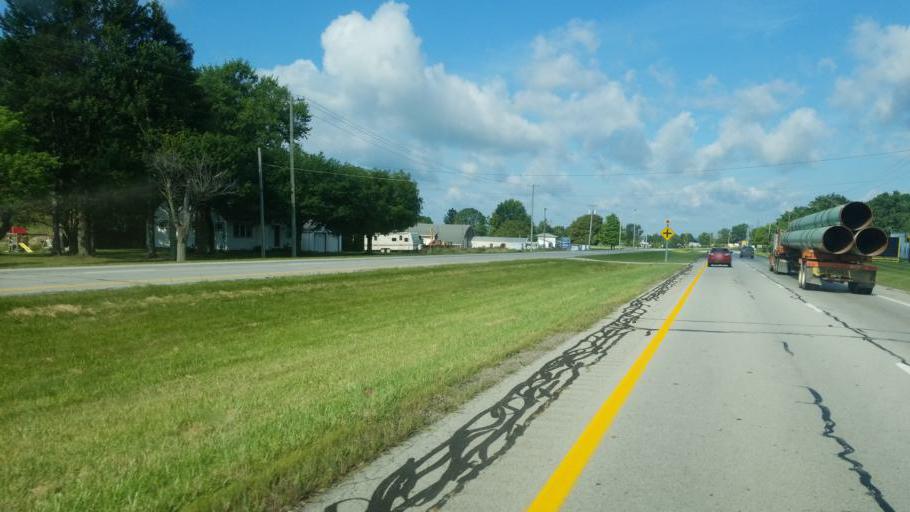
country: US
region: Ohio
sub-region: Wayne County
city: Dalton
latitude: 40.8007
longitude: -81.7219
